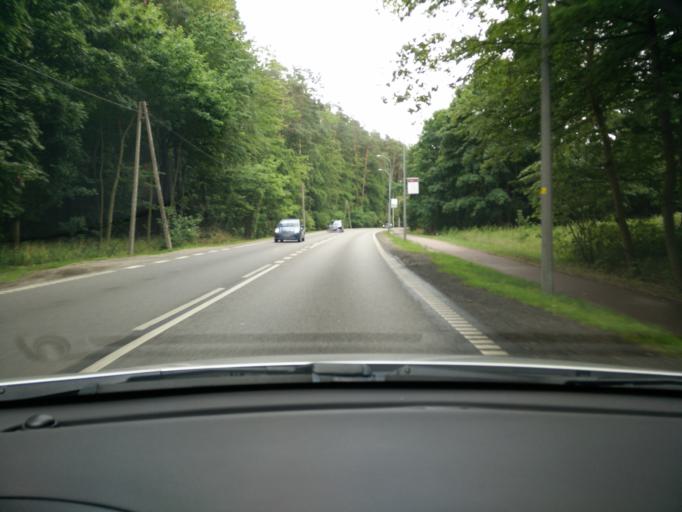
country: PL
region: Pomeranian Voivodeship
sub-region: Sopot
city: Sopot
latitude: 54.4153
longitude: 18.5459
